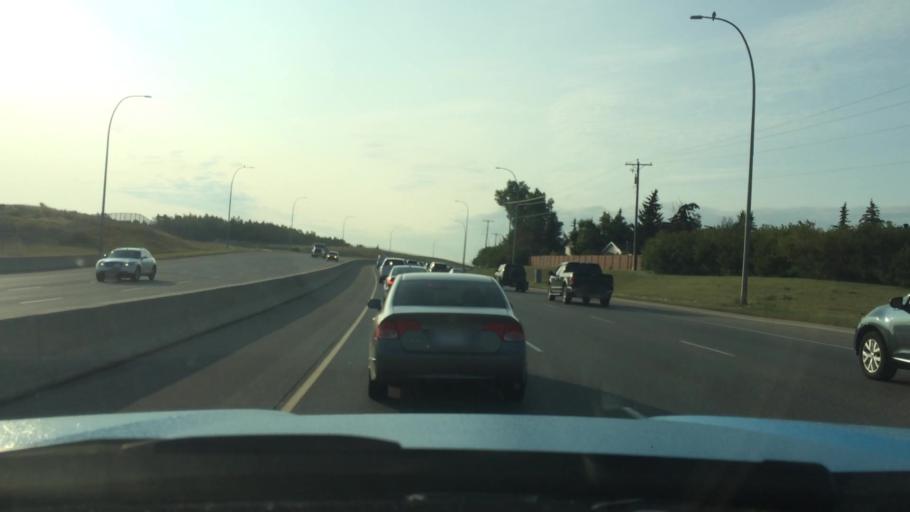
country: CA
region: Alberta
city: Calgary
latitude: 51.1307
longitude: -114.0620
